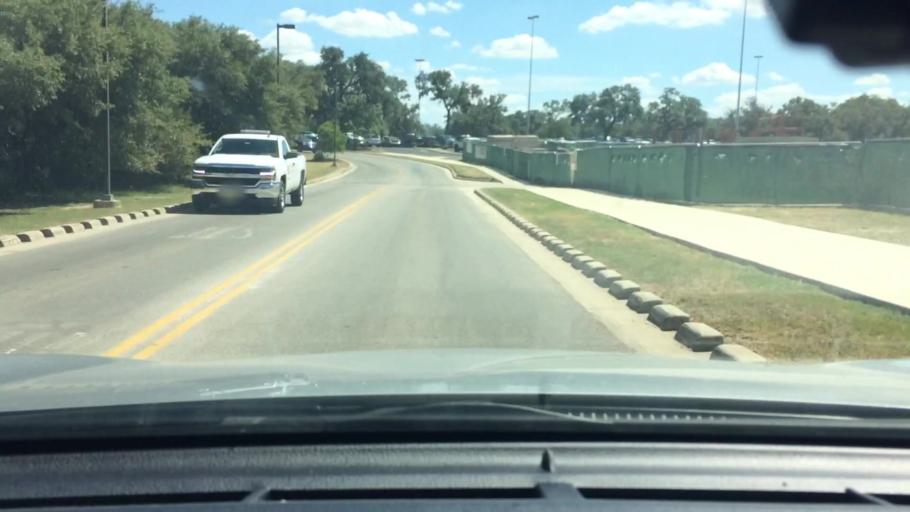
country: US
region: Texas
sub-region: Bexar County
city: Shavano Park
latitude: 29.5827
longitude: -98.6149
